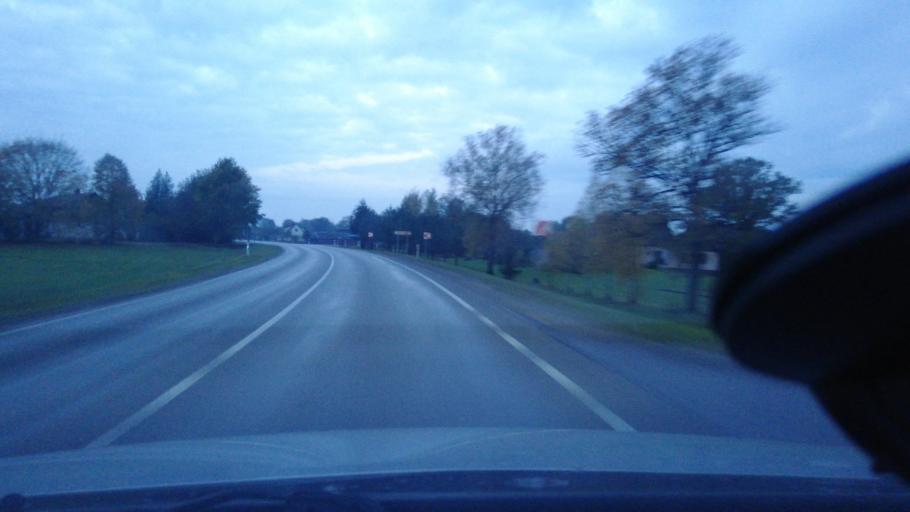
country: LT
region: Telsiu apskritis
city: Plunge
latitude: 55.8828
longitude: 21.7708
